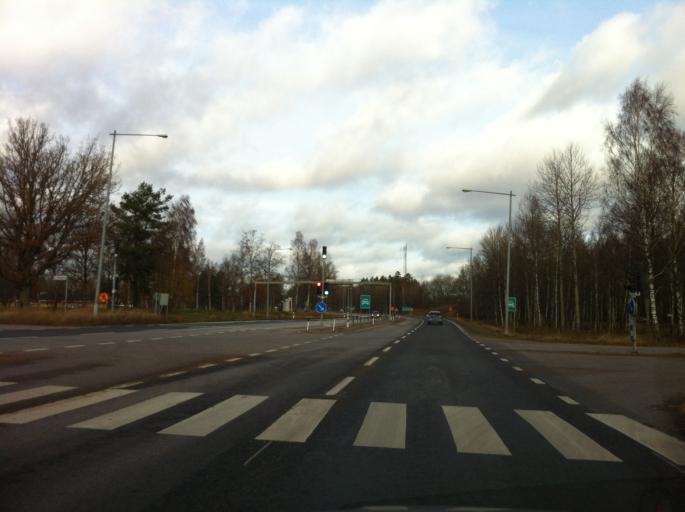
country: SE
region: Kronoberg
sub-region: Vaxjo Kommun
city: Gemla
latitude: 56.8059
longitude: 14.6567
